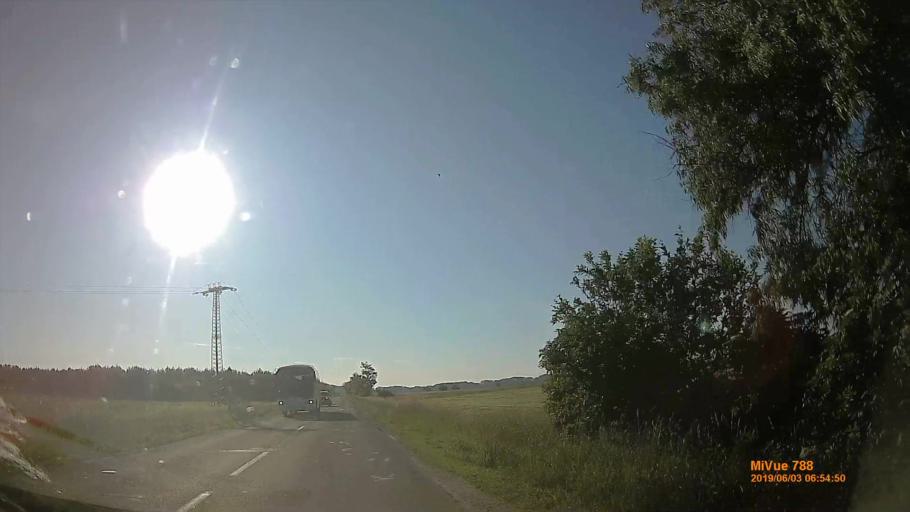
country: HU
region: Pest
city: Ocsa
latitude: 47.2167
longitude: 19.2321
